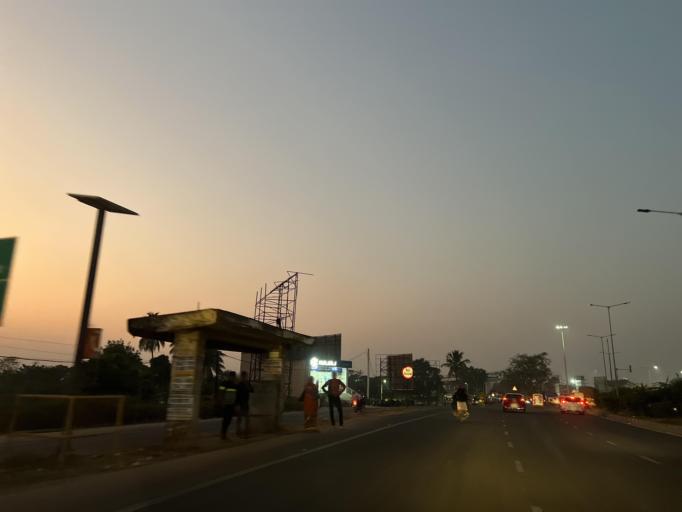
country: IN
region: Odisha
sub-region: Cuttack
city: Cuttack
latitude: 20.4270
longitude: 85.8778
